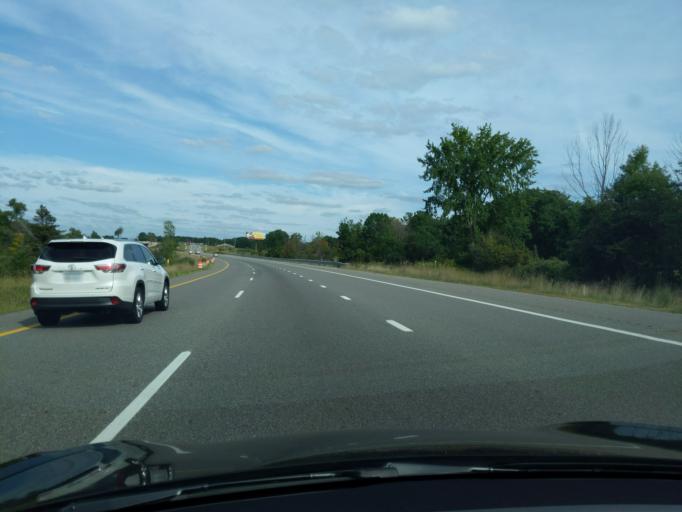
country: US
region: Michigan
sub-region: Muskegon County
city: Fruitport
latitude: 43.0719
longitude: -86.0749
